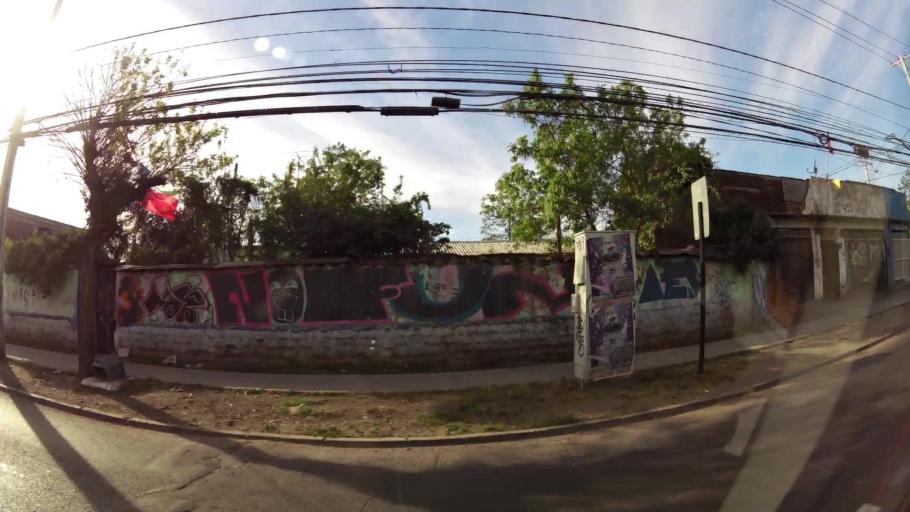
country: CL
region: Santiago Metropolitan
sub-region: Provincia de Cordillera
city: Puente Alto
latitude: -33.6132
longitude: -70.5832
